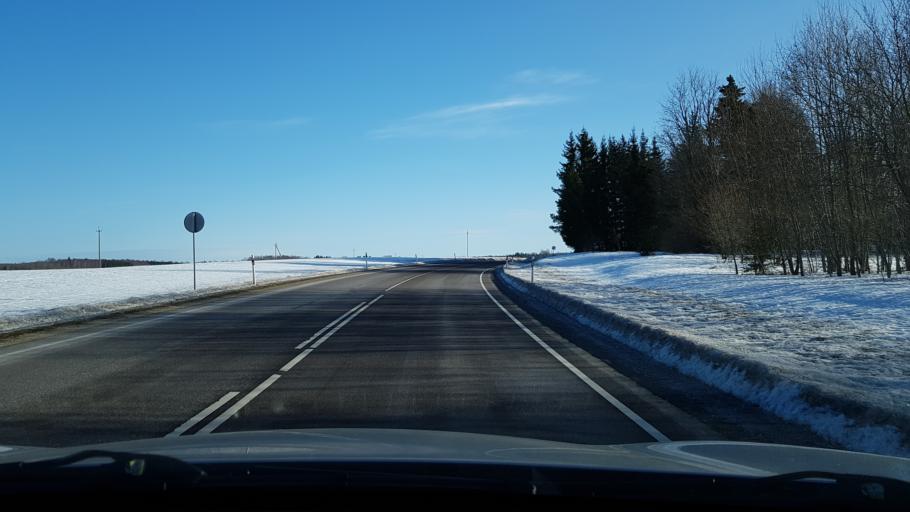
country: EE
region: Jogevamaa
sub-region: Poltsamaa linn
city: Poltsamaa
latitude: 58.6385
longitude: 25.7618
